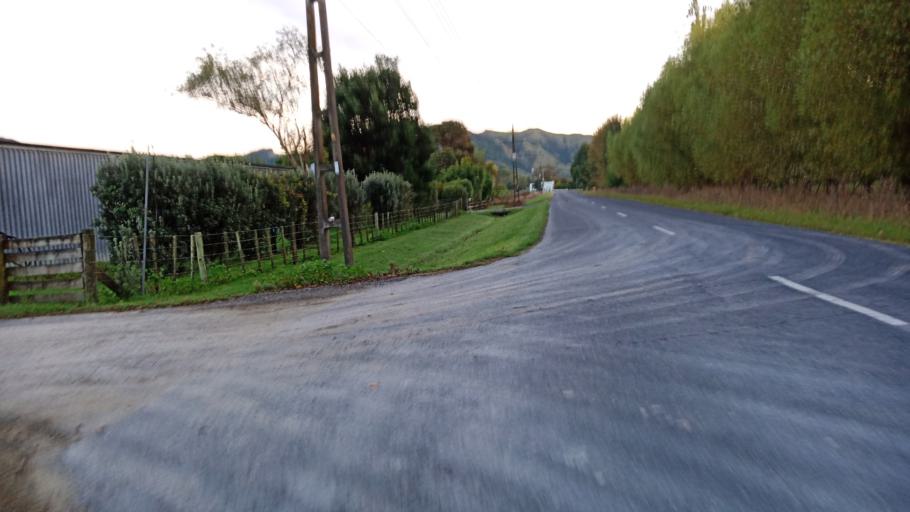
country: NZ
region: Gisborne
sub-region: Gisborne District
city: Gisborne
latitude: -38.6226
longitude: 177.9794
